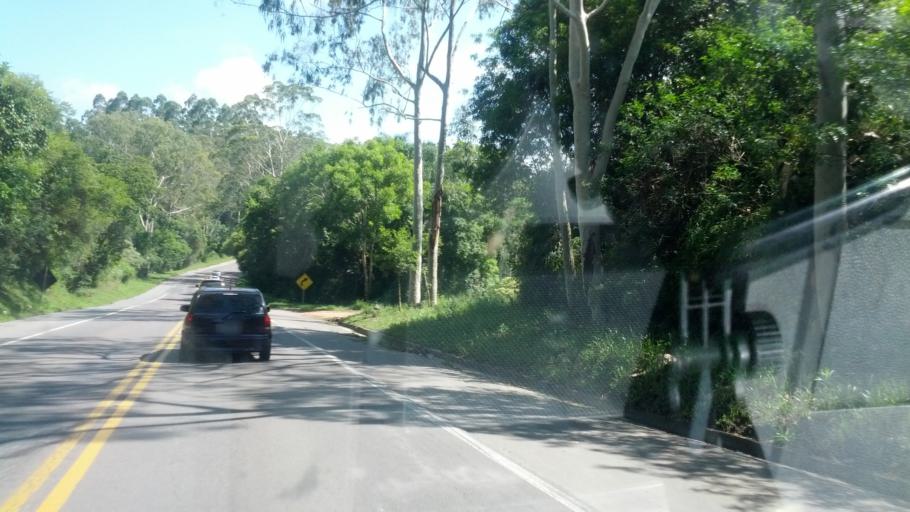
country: BR
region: Santa Catarina
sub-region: Ibirama
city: Ibirama
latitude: -27.1447
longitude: -49.5489
